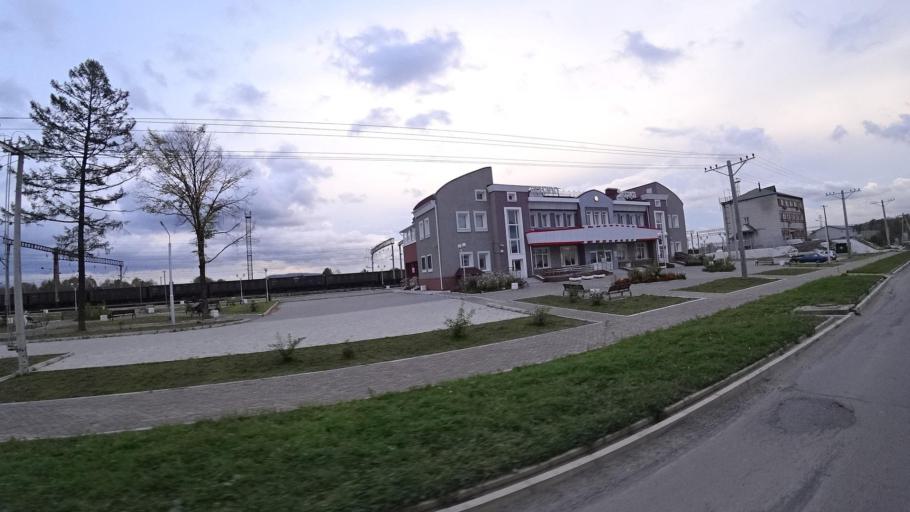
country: RU
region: Jewish Autonomous Oblast
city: Izvestkovyy
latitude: 48.9831
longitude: 131.5559
